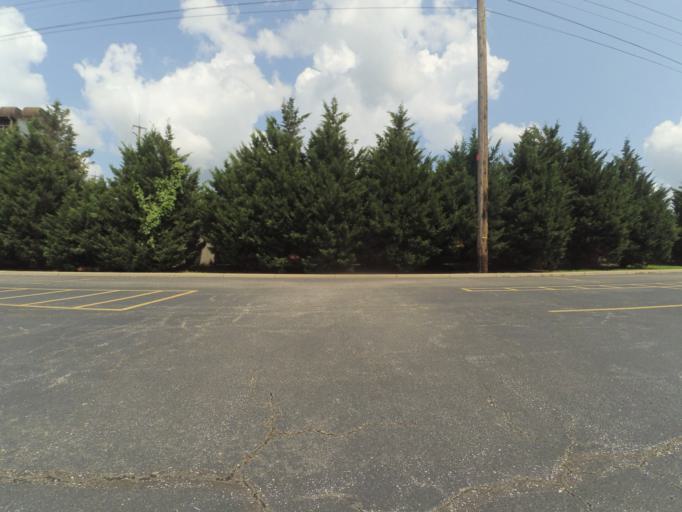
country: US
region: West Virginia
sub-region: Cabell County
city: Huntington
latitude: 38.4253
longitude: -82.4308
